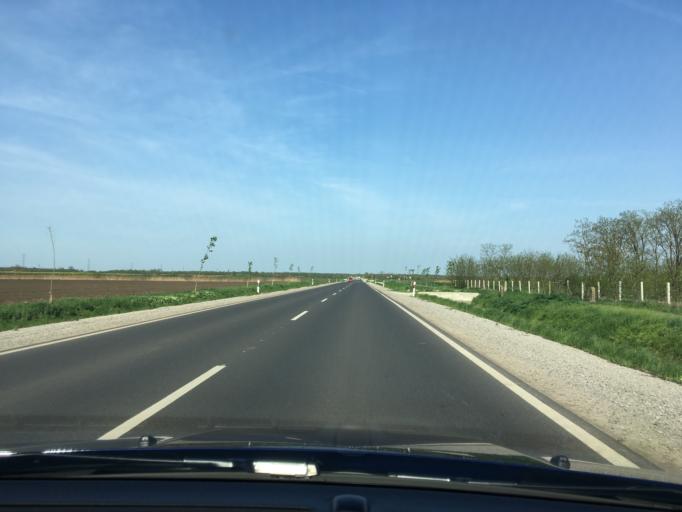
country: HU
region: Bekes
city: Csorvas
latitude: 46.6410
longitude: 20.8530
